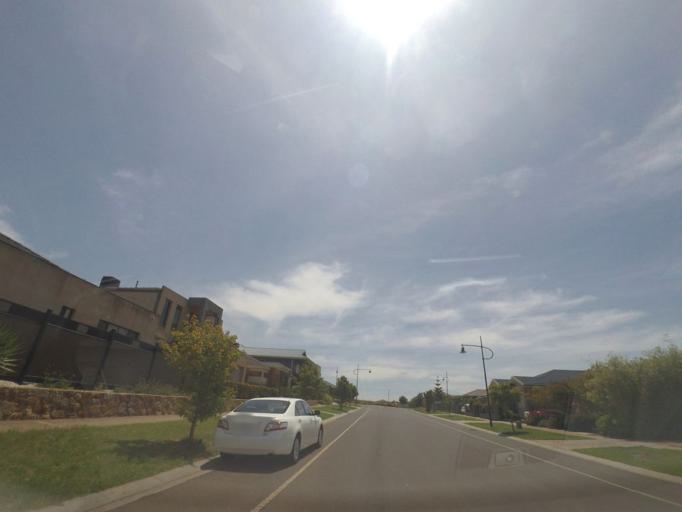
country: AU
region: Victoria
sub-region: Hume
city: Roxburgh Park
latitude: -37.6114
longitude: 144.9083
